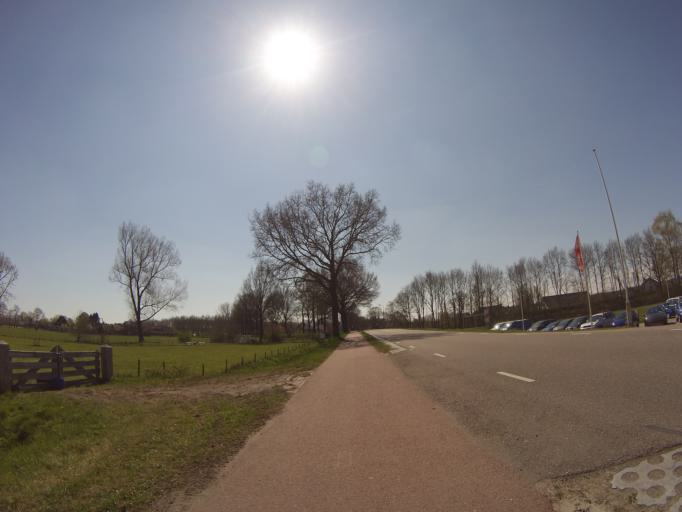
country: NL
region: Utrecht
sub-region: Gemeente Utrechtse Heuvelrug
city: Overberg
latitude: 52.0417
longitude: 5.4910
